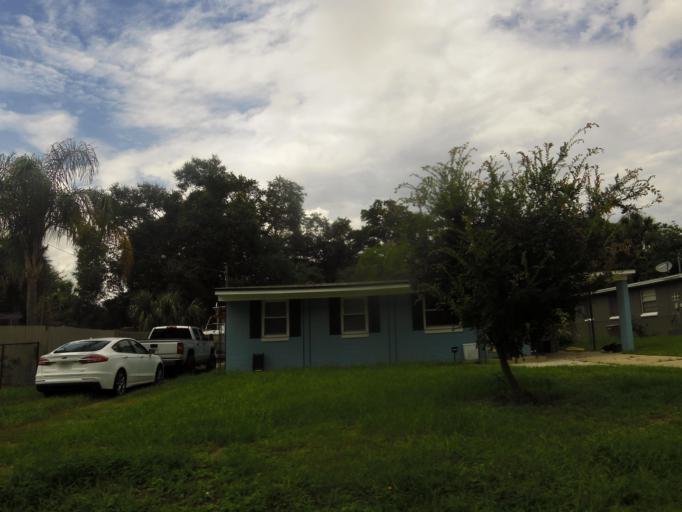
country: US
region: Florida
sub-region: Duval County
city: Jacksonville
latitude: 30.2845
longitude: -81.5569
